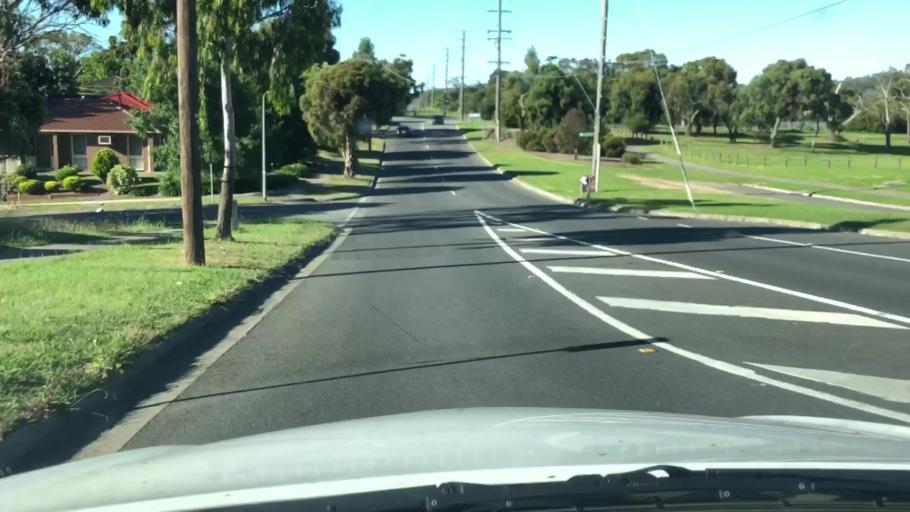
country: AU
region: Victoria
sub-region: Casey
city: Endeavour Hills
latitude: -37.9668
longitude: 145.2434
